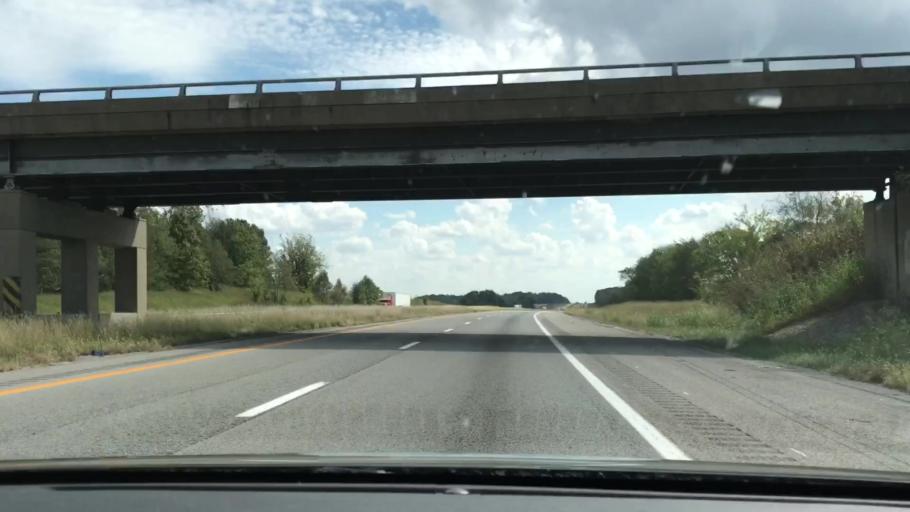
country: US
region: Kentucky
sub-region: Christian County
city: Hopkinsville
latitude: 36.7875
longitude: -87.5856
